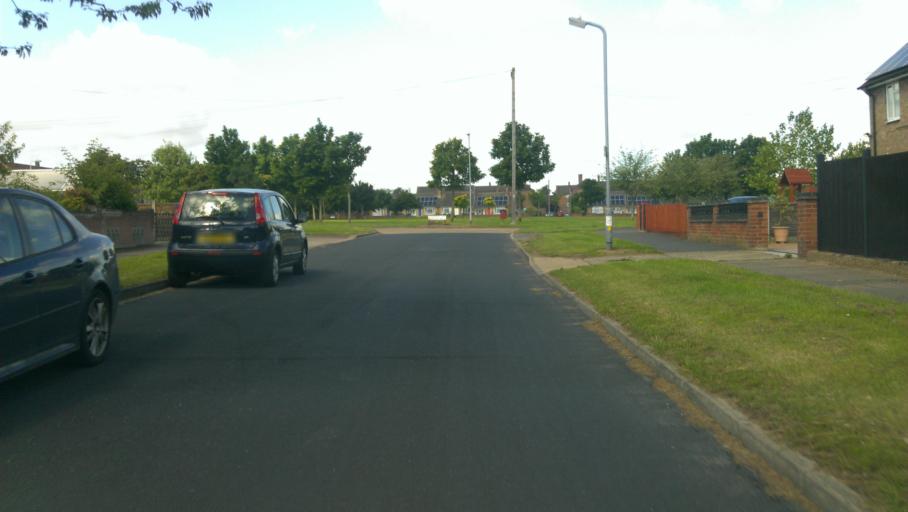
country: GB
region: England
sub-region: Essex
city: Colchester
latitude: 51.8752
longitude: 0.9171
